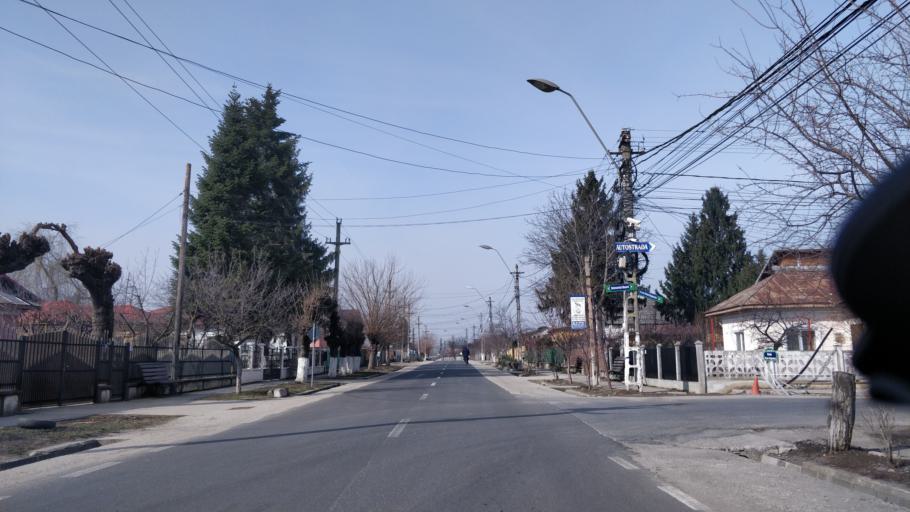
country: RO
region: Giurgiu
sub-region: Comuna Bolintin Deal
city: Bolintin Deal
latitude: 44.4582
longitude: 25.8172
